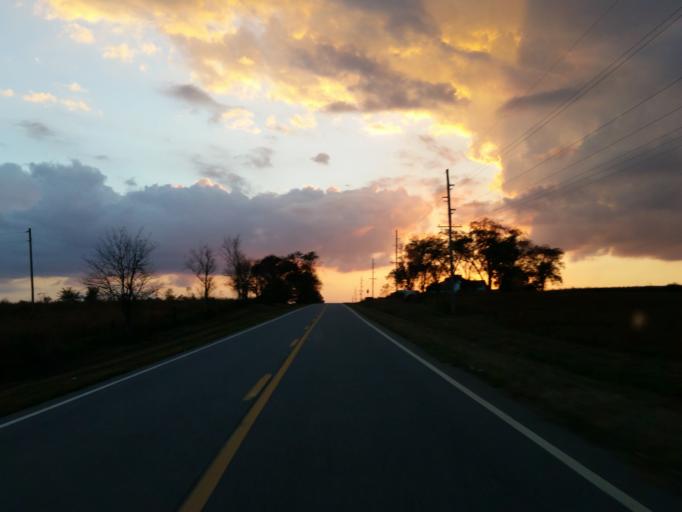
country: US
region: Georgia
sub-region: Dooly County
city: Unadilla
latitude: 32.1527
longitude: -83.6496
